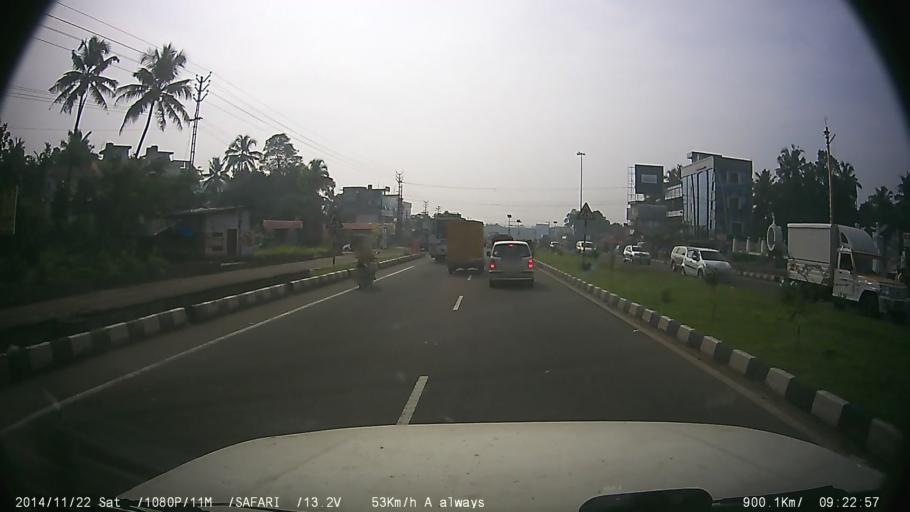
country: IN
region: Kerala
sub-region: Ernakulam
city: Angamali
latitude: 10.2123
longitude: 76.3807
